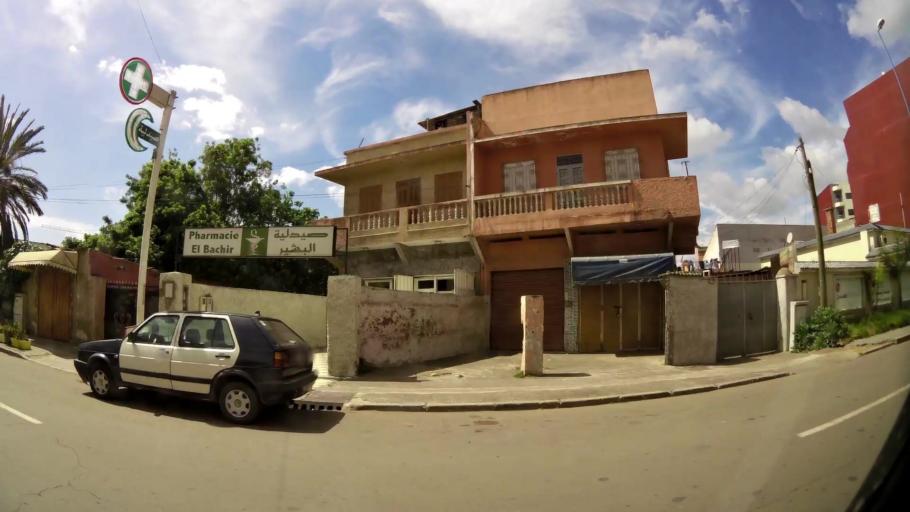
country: MA
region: Grand Casablanca
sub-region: Casablanca
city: Casablanca
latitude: 33.6160
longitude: -7.5391
